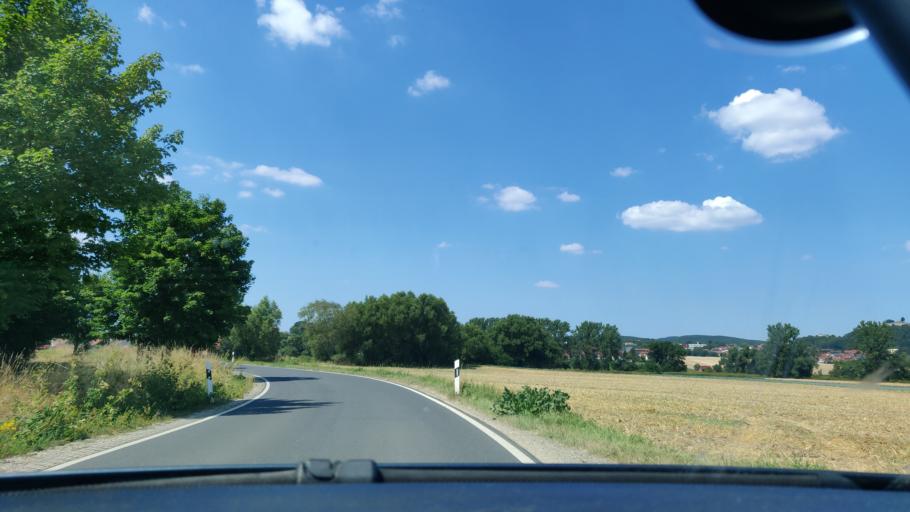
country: DE
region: Hesse
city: Gudensberg
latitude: 51.1549
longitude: 9.3606
